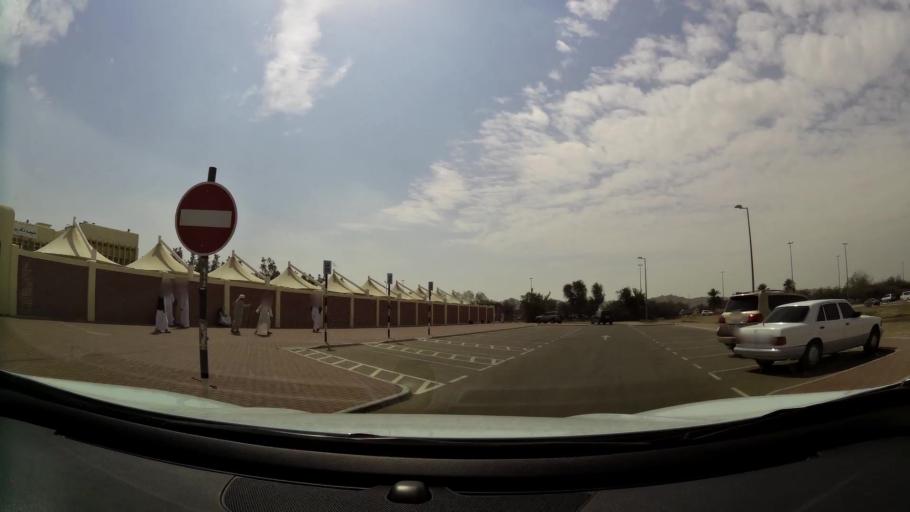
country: AE
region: Abu Dhabi
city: Al Ain
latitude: 24.1932
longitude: 55.7905
